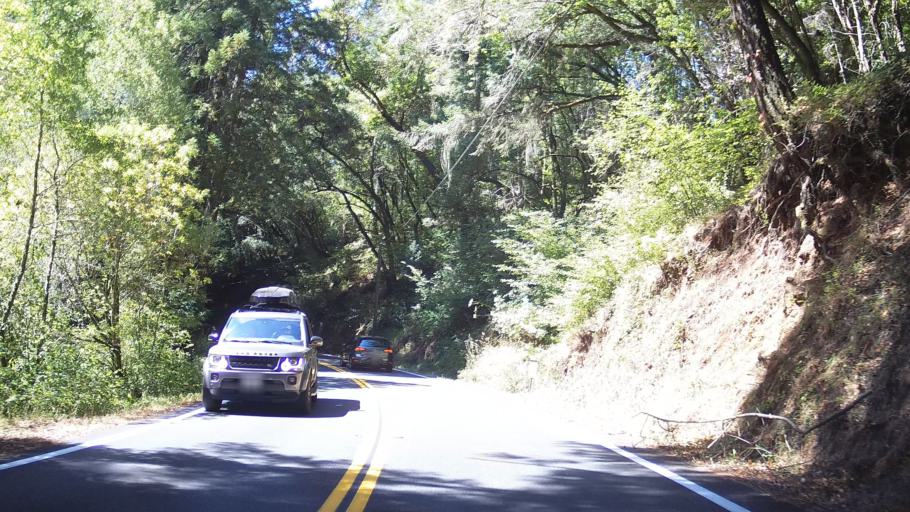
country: US
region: California
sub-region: Marin County
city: Lagunitas-Forest Knolls
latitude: 38.0187
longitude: -122.7241
